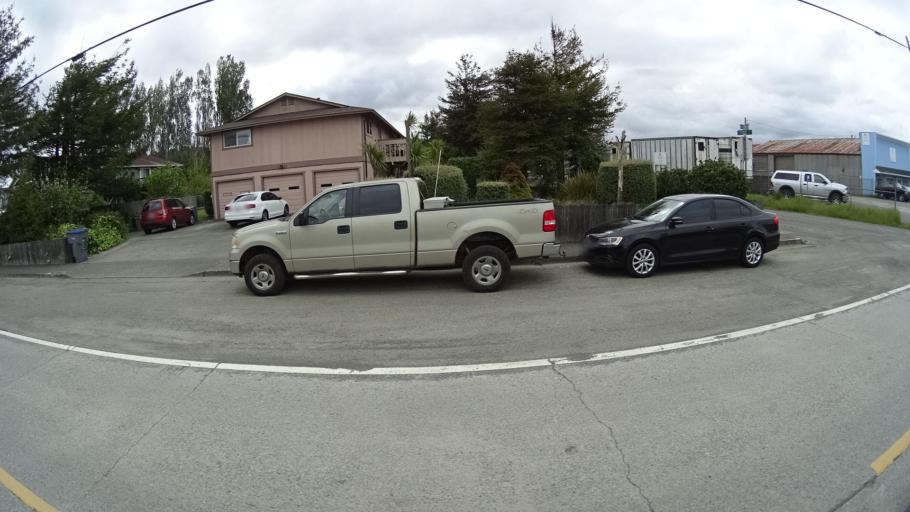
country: US
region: California
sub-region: Humboldt County
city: Arcata
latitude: 40.8612
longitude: -124.0887
